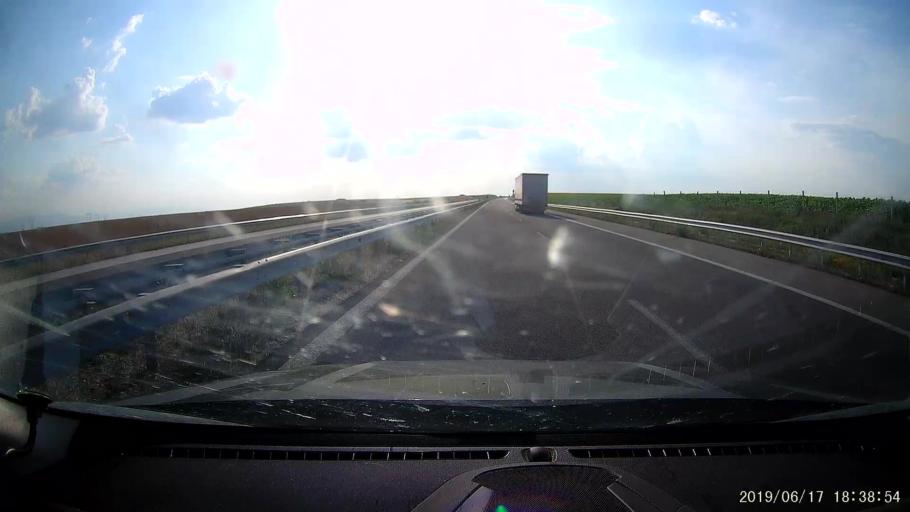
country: BG
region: Stara Zagora
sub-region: Obshtina Chirpan
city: Chirpan
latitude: 42.1402
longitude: 25.3236
